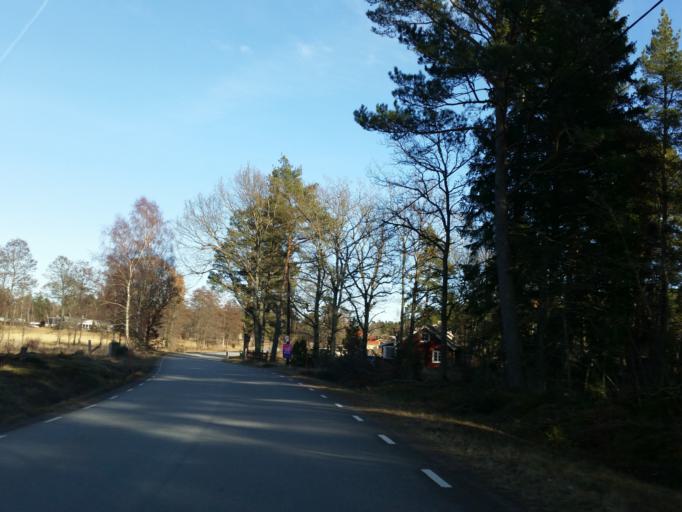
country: SE
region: Kalmar
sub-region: Kalmar Kommun
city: Lindsdal
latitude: 56.7843
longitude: 16.3891
